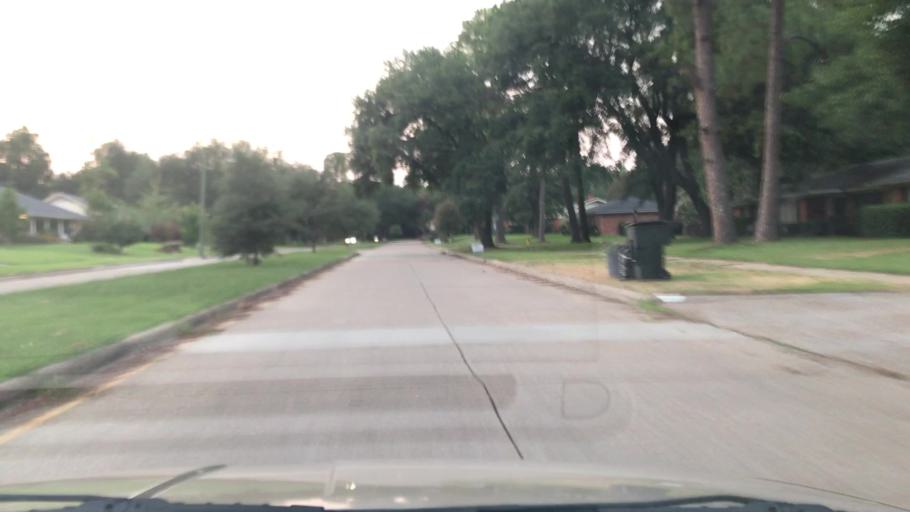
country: US
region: Louisiana
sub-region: Bossier Parish
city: Bossier City
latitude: 32.4524
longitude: -93.7316
